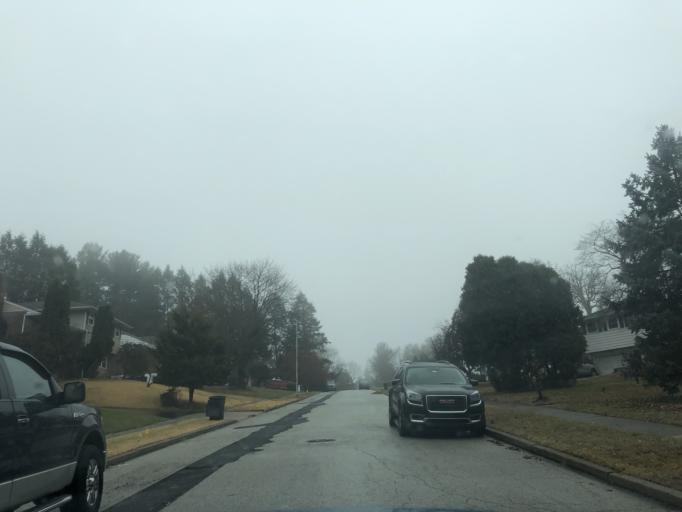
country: US
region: Pennsylvania
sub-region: Delaware County
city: Broomall
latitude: 39.9845
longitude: -75.3450
